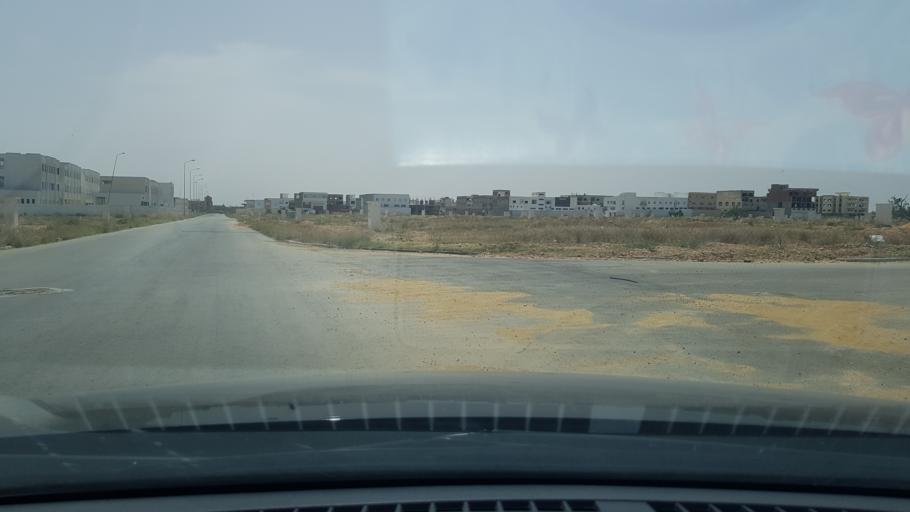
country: TN
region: Safaqis
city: Al Qarmadah
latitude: 34.8274
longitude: 10.7449
